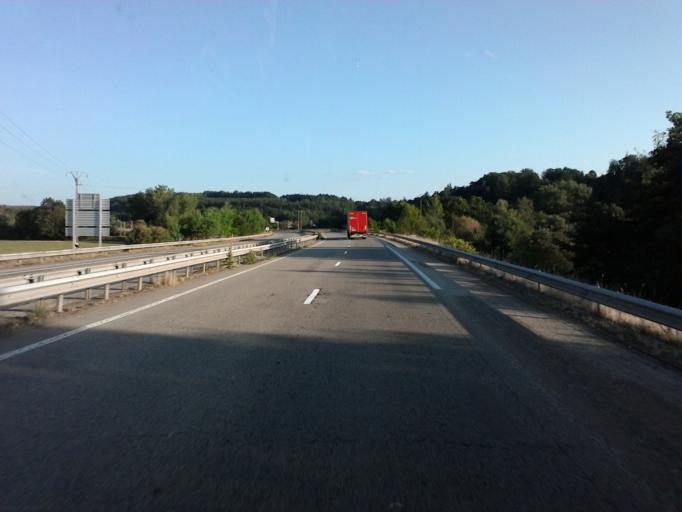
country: FR
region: Lorraine
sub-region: Departement des Vosges
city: Arches
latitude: 48.1306
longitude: 6.5150
